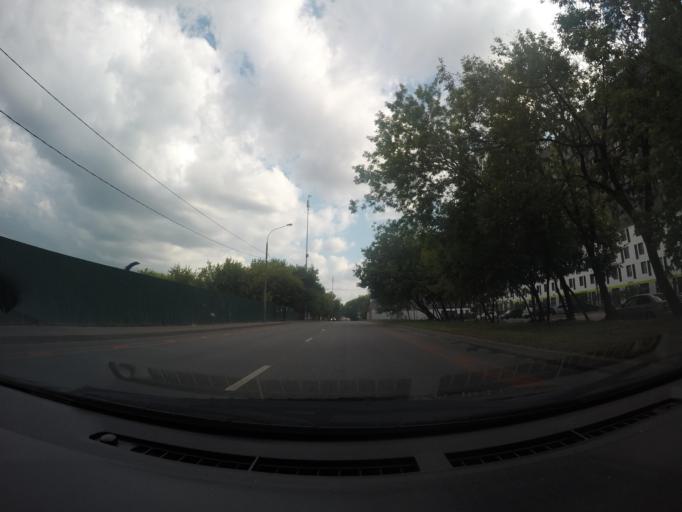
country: RU
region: Moscow
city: Sviblovo
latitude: 55.8549
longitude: 37.6258
